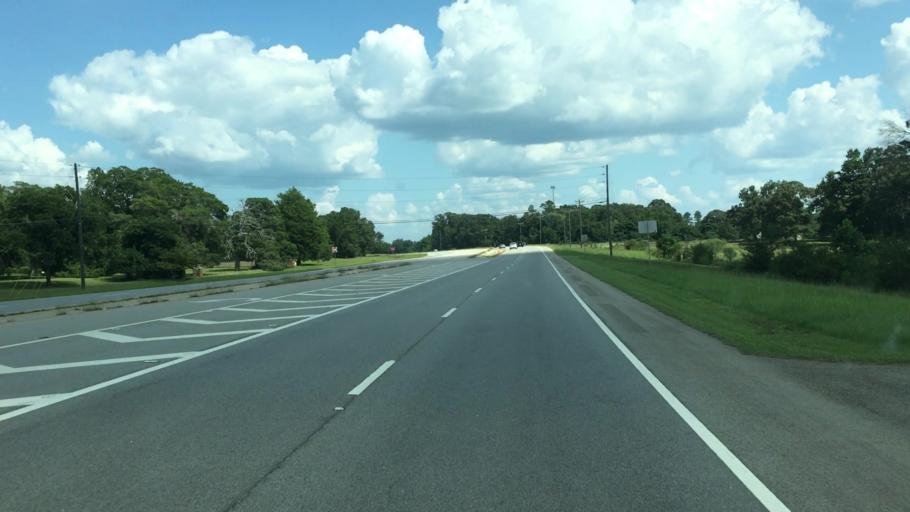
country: US
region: Georgia
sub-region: Putnam County
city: Eatonton
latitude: 33.2714
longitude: -83.3461
